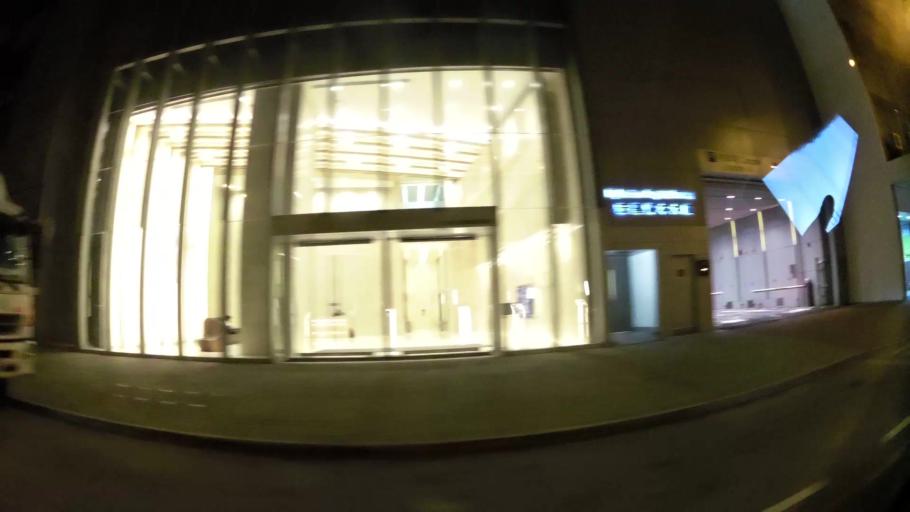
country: HK
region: Kowloon City
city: Kowloon
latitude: 22.3126
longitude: 114.2176
